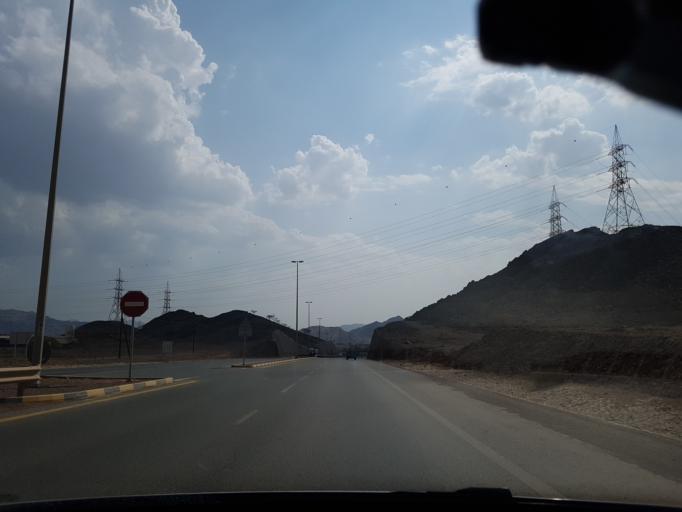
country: AE
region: Al Fujayrah
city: Dibba Al-Fujairah
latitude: 25.5044
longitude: 56.0735
